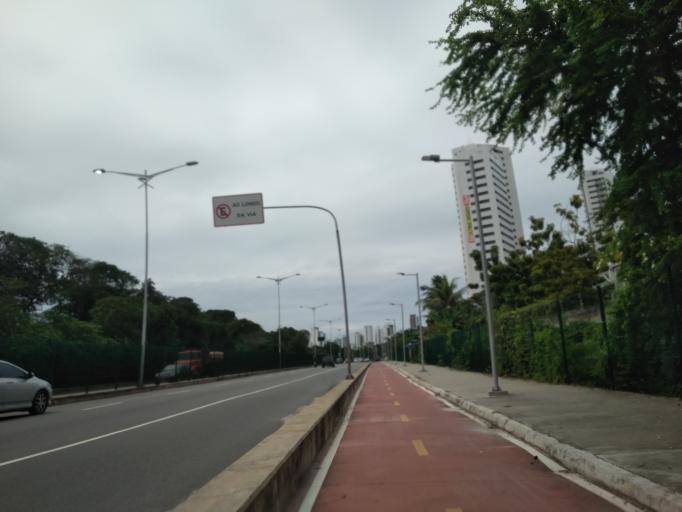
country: BR
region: Pernambuco
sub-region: Recife
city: Recife
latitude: -8.1072
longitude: -34.8936
